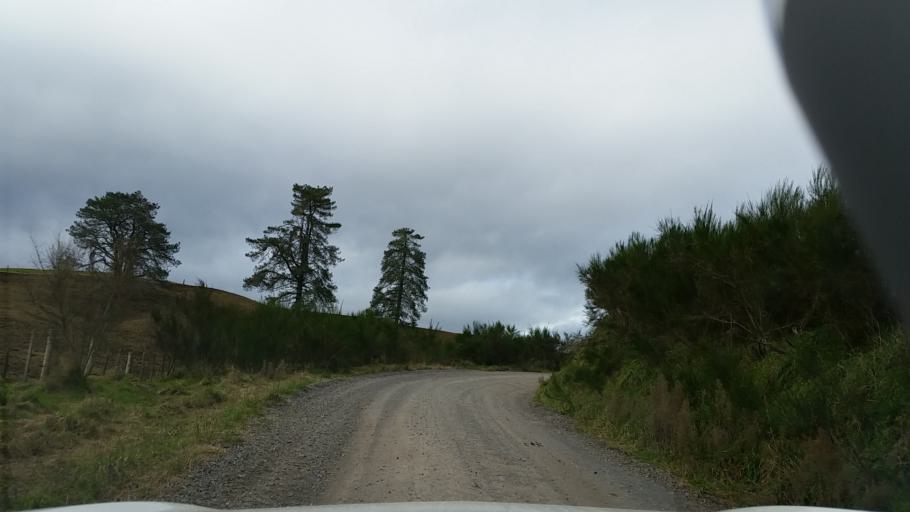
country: NZ
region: Bay of Plenty
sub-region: Whakatane District
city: Murupara
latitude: -38.3405
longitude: 176.5401
